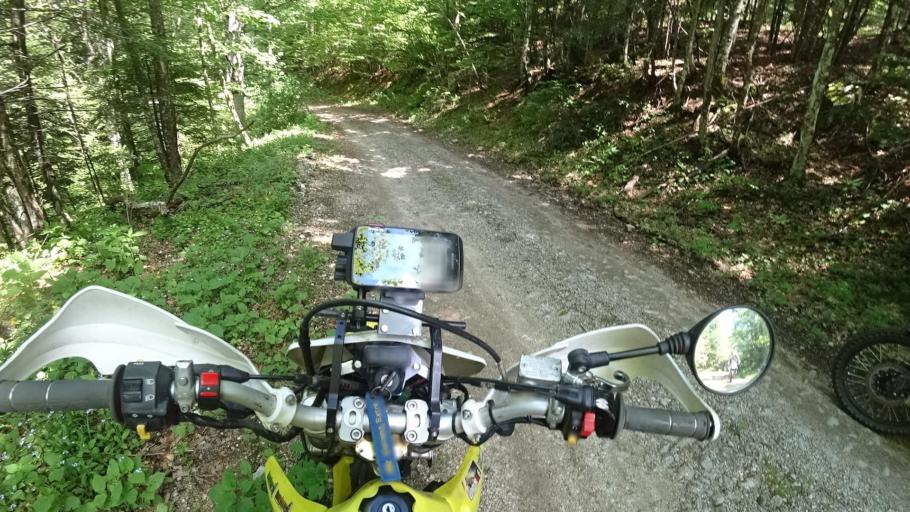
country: BA
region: Federation of Bosnia and Herzegovina
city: Bosanska Krupa
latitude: 44.8106
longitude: 16.0680
